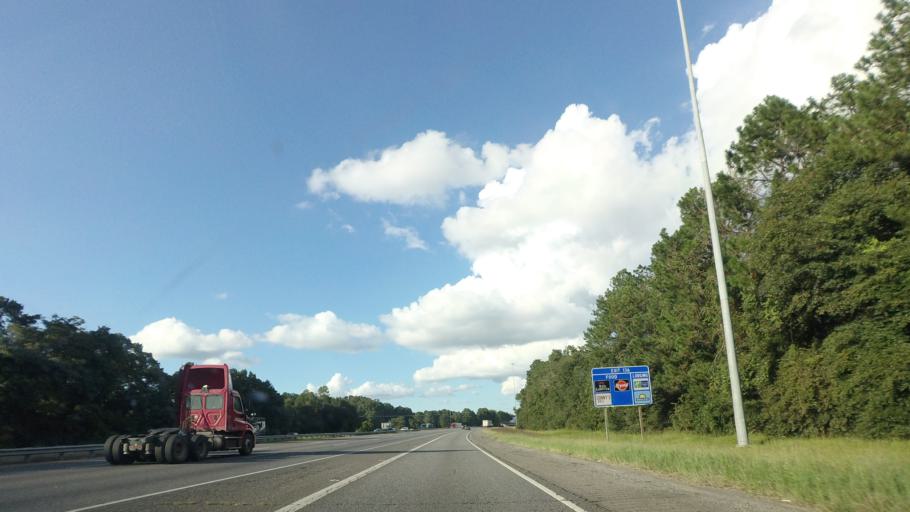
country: US
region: Georgia
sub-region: Houston County
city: Perry
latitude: 32.4506
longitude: -83.7538
